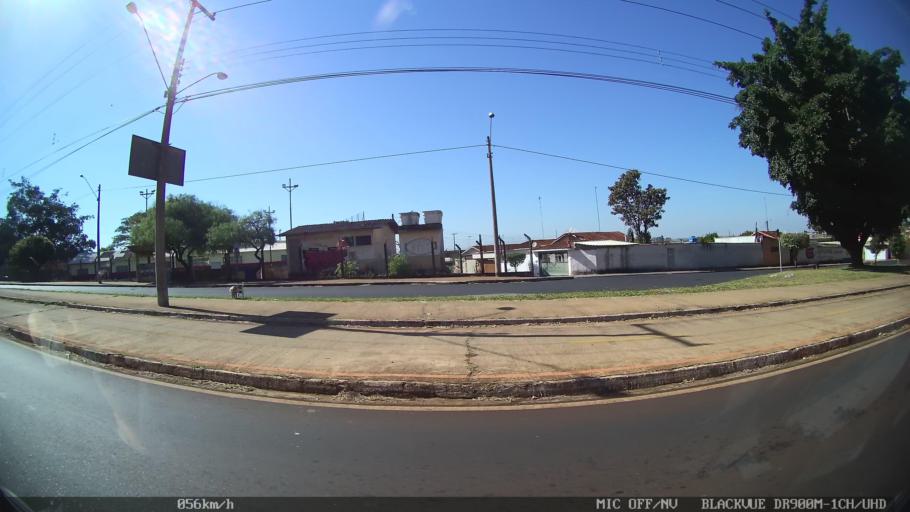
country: BR
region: Sao Paulo
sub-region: Batatais
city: Batatais
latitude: -20.9041
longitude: -47.5819
